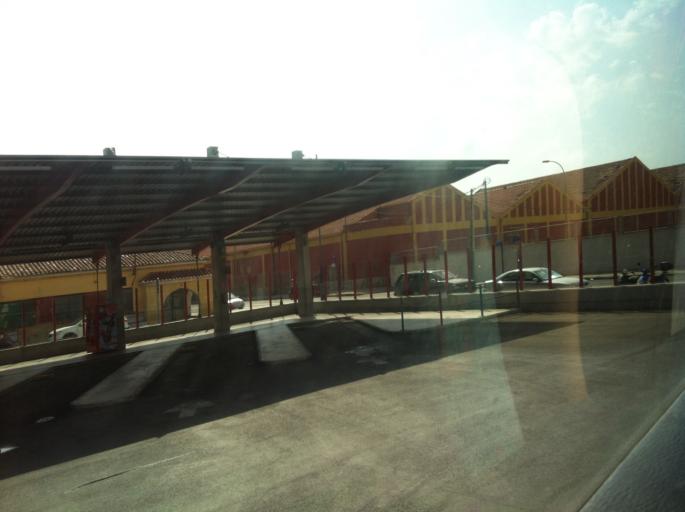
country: ES
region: Valencia
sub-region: Provincia de Alicante
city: Alicante
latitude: 38.3371
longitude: -0.4913
